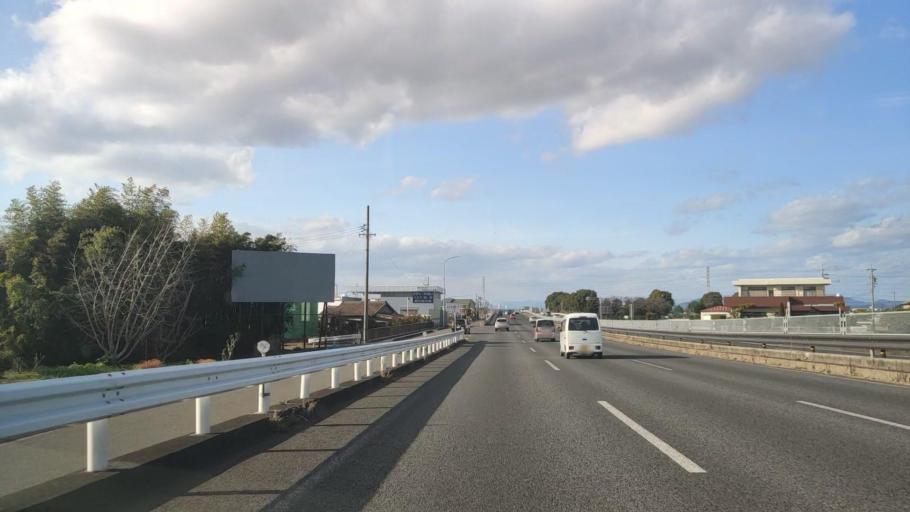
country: JP
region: Aichi
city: Ichinomiya
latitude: 35.3275
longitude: 136.8056
